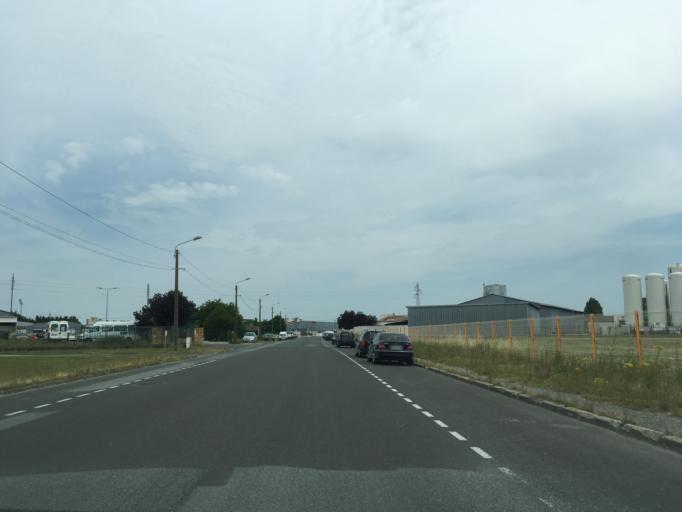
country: FR
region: Poitou-Charentes
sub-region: Departement des Deux-Sevres
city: Bessines
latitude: 46.3127
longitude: -0.4958
